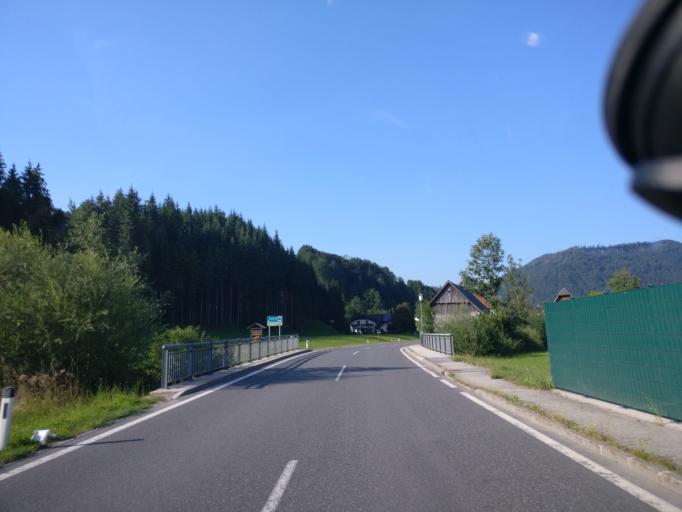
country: AT
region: Lower Austria
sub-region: Politischer Bezirk Scheibbs
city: Gostling an der Ybbs
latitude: 47.7935
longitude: 14.9192
